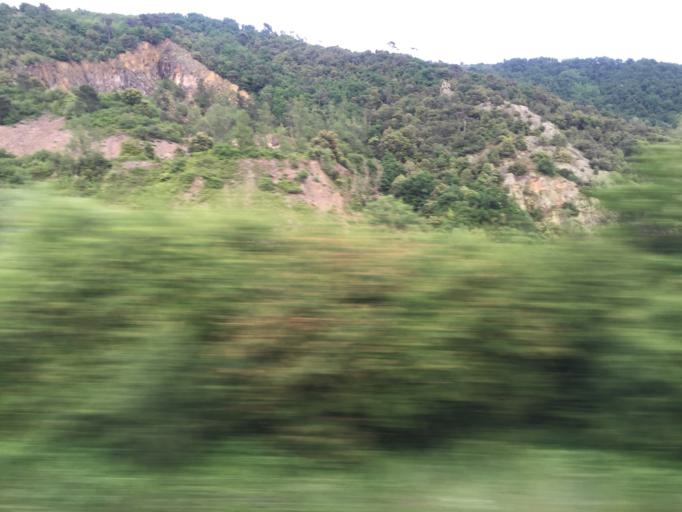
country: FR
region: Rhone-Alpes
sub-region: Departement de la Drome
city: Saint-Vallier
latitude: 45.1354
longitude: 4.8179
